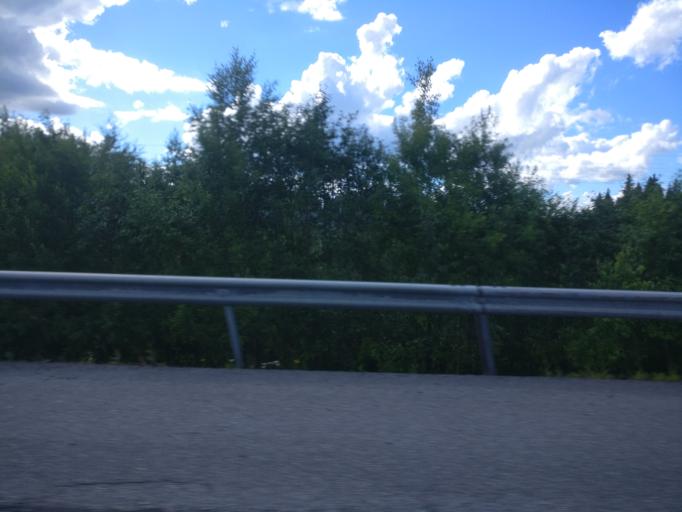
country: FI
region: Uusimaa
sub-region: Porvoo
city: Pukkila
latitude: 60.7545
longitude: 25.4594
